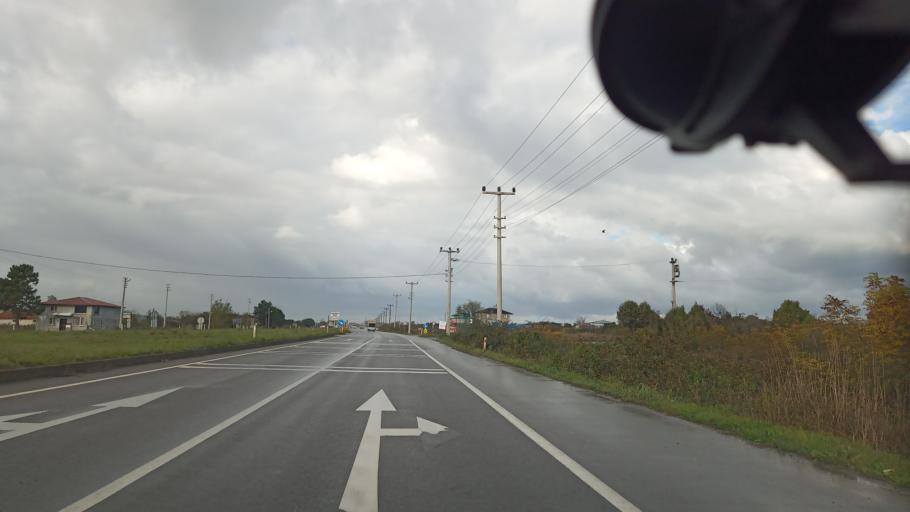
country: TR
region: Sakarya
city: Karasu
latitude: 41.0822
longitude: 30.7643
